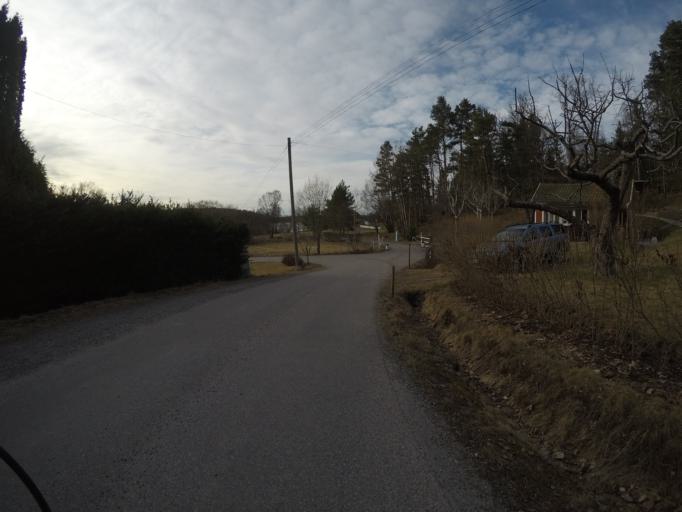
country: SE
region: Soedermanland
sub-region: Eskilstuna Kommun
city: Hallbybrunn
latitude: 59.4353
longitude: 16.4133
